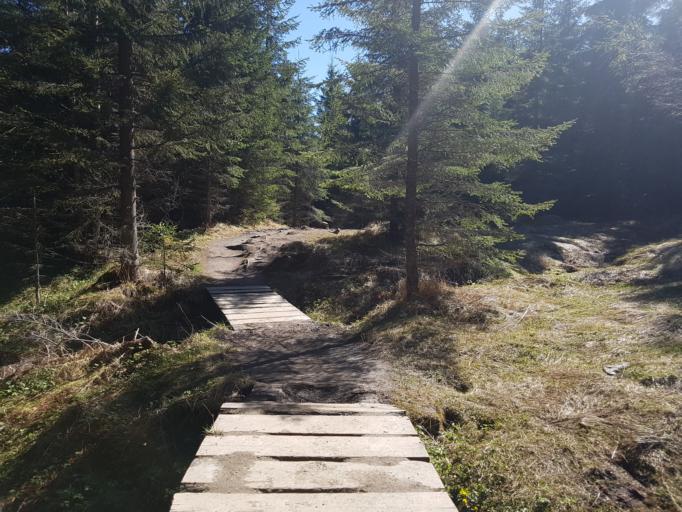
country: NO
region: Sor-Trondelag
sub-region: Trondheim
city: Trondheim
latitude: 63.4252
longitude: 10.3140
